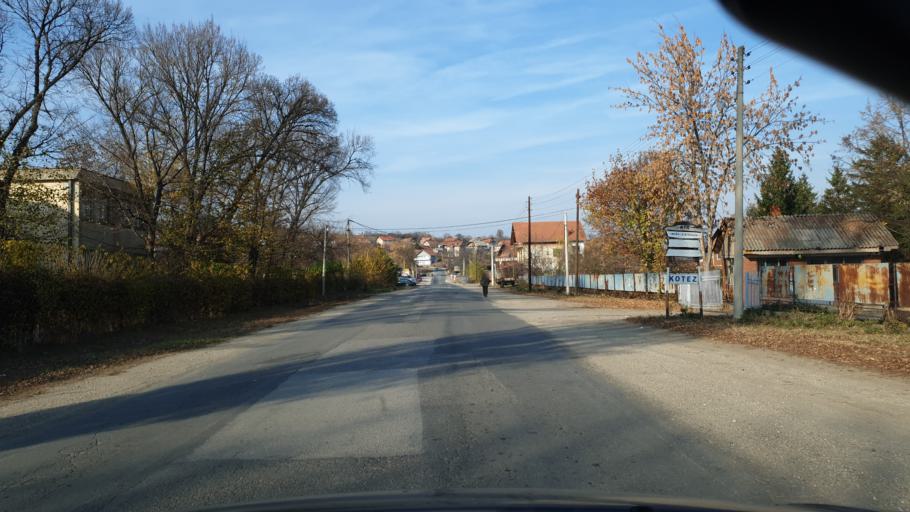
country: RS
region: Central Serbia
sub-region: Zajecarski Okrug
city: Zajecar
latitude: 43.9158
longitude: 22.2907
